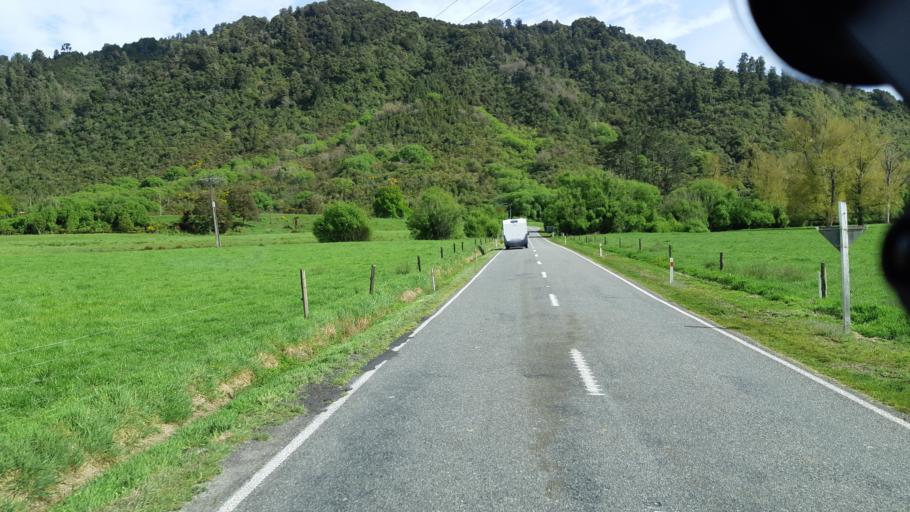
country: NZ
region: West Coast
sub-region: Buller District
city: Westport
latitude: -41.8602
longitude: 171.9398
